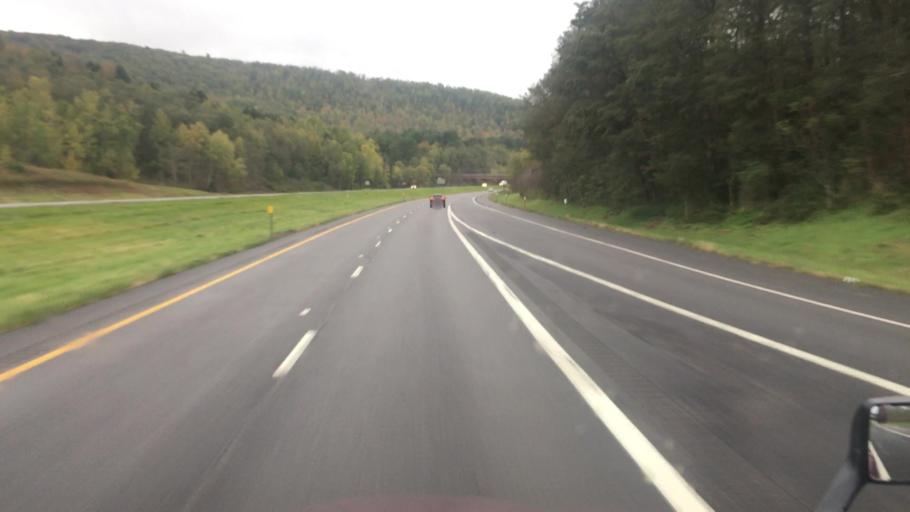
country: US
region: New York
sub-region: Otsego County
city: Unadilla
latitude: 42.3116
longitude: -75.3278
